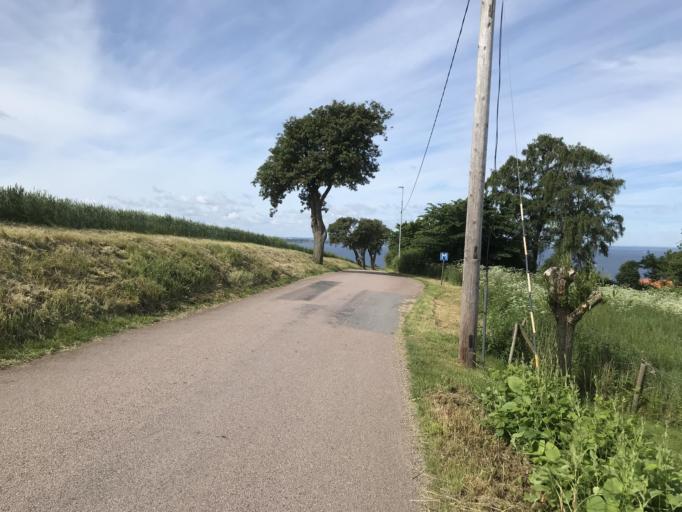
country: SE
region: Skane
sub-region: Helsingborg
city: Glumslov
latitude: 55.9340
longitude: 12.7995
